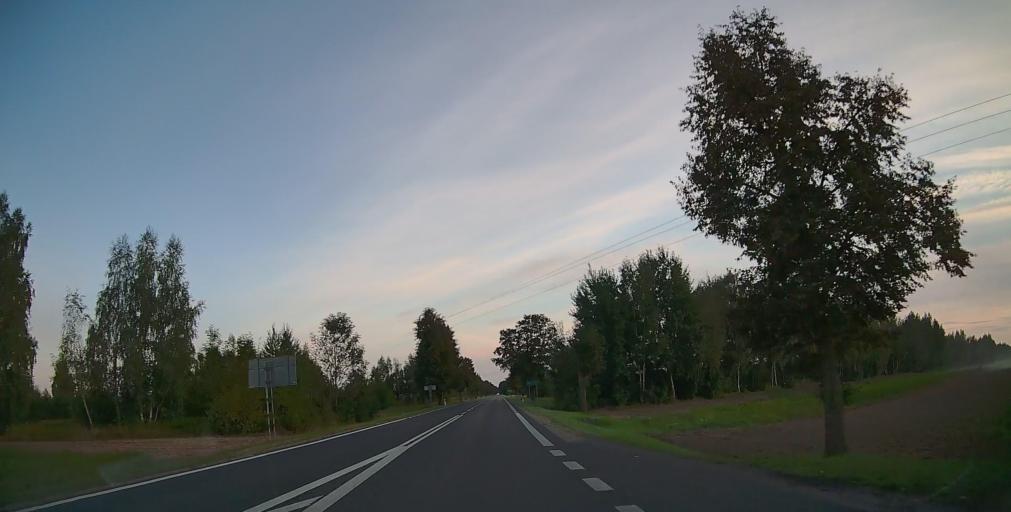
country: PL
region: Masovian Voivodeship
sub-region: Powiat kozienicki
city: Ryczywol
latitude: 51.7500
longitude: 21.3854
